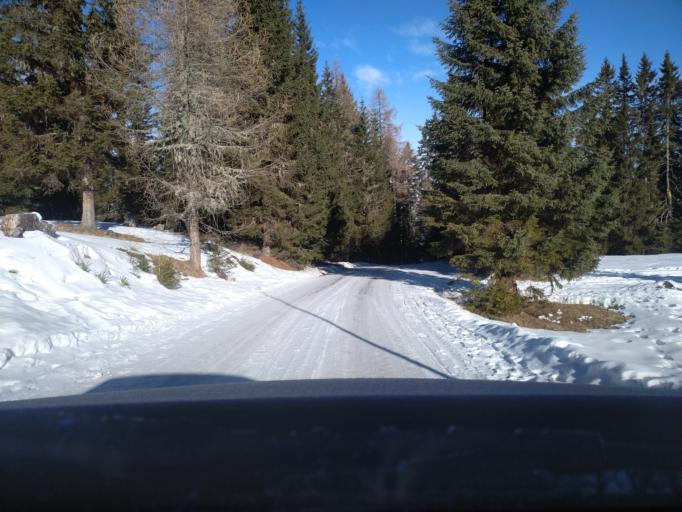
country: AT
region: Carinthia
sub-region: Politischer Bezirk Villach Land
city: Arriach
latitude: 46.6989
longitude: 13.8952
